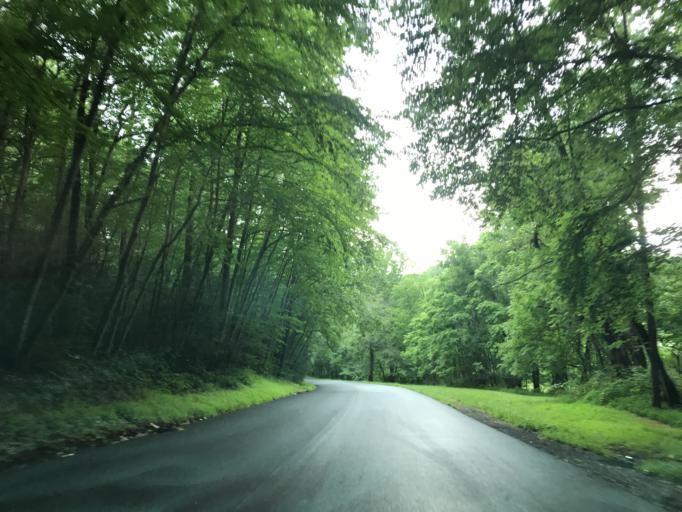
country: US
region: Pennsylvania
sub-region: York County
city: New Freedom
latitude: 39.6823
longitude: -76.7641
